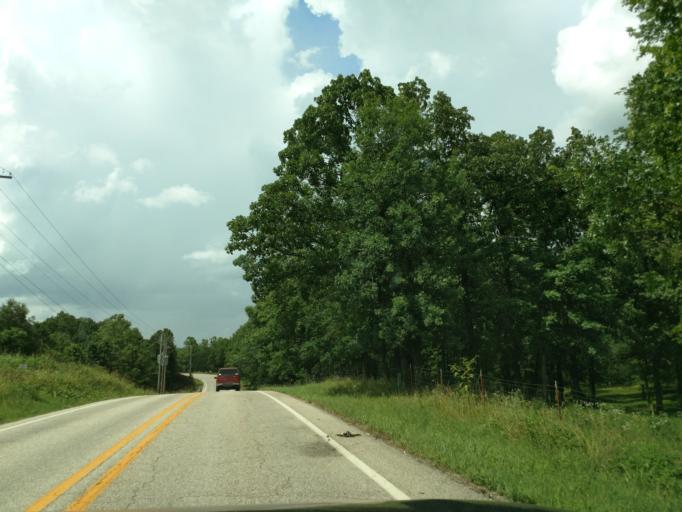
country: US
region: Arkansas
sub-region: Boone County
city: Harrison
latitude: 36.2856
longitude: -93.2355
